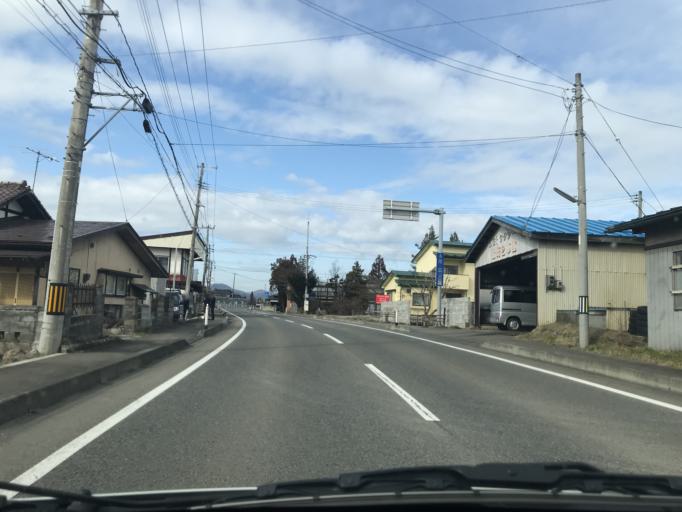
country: JP
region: Iwate
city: Hanamaki
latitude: 39.3615
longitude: 141.0510
